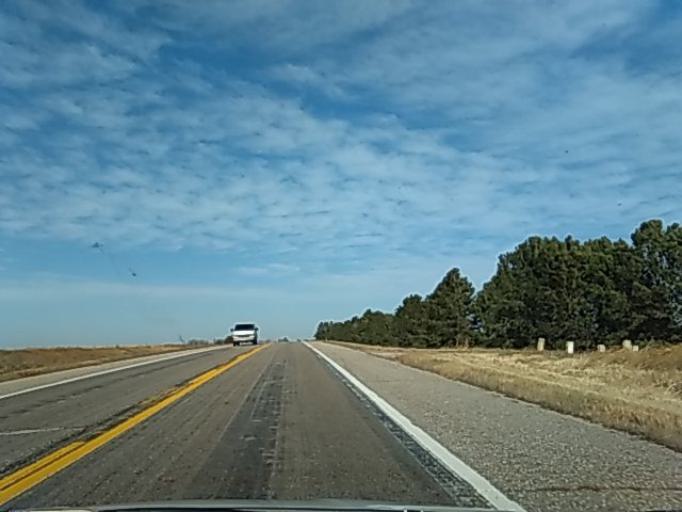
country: US
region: Nebraska
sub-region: Clay County
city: Clay Center
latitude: 40.4764
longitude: -98.0515
